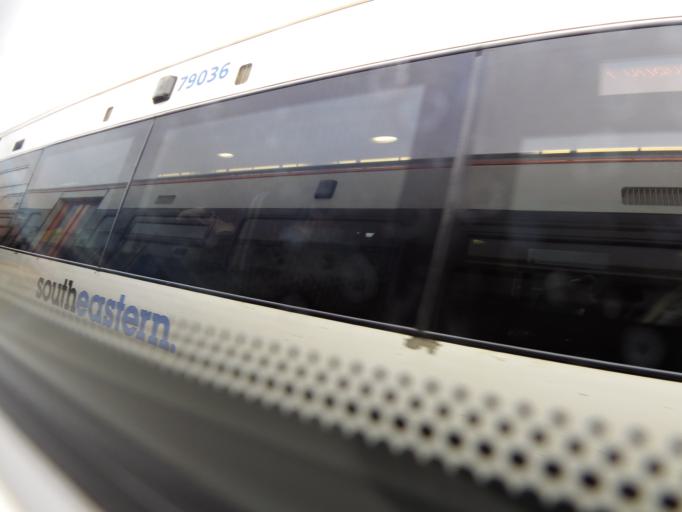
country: GB
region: England
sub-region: Greater London
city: Thornton Heath
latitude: 51.3949
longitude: -0.0762
